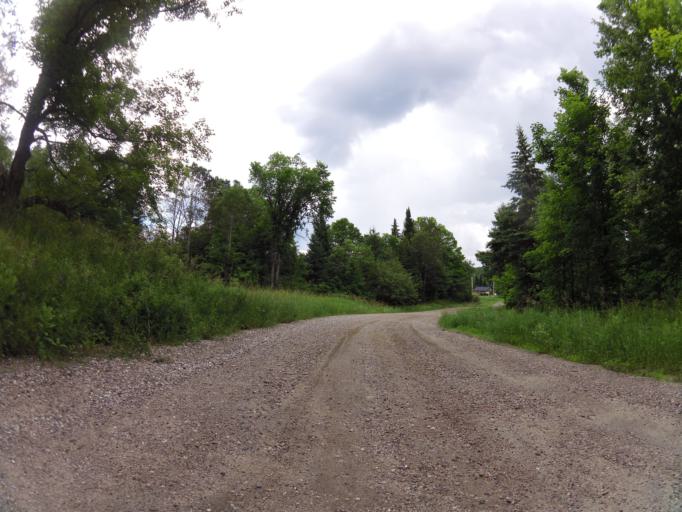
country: CA
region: Ontario
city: Renfrew
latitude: 45.0651
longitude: -76.7569
